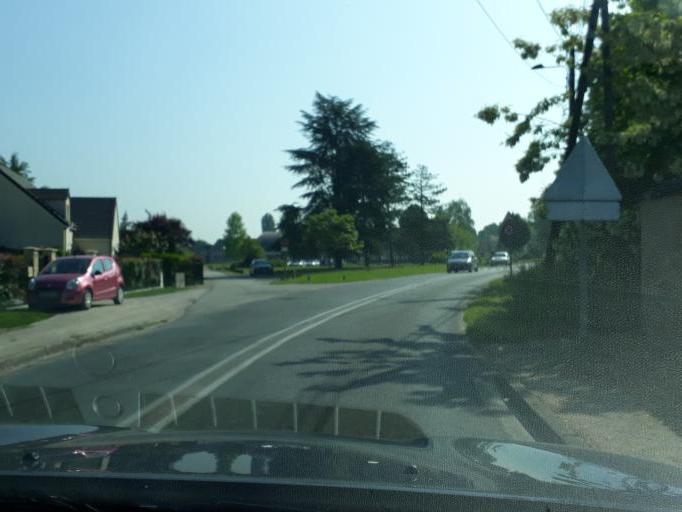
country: FR
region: Centre
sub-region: Departement du Loiret
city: Boigny-sur-Bionne
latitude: 47.9215
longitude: 2.0135
